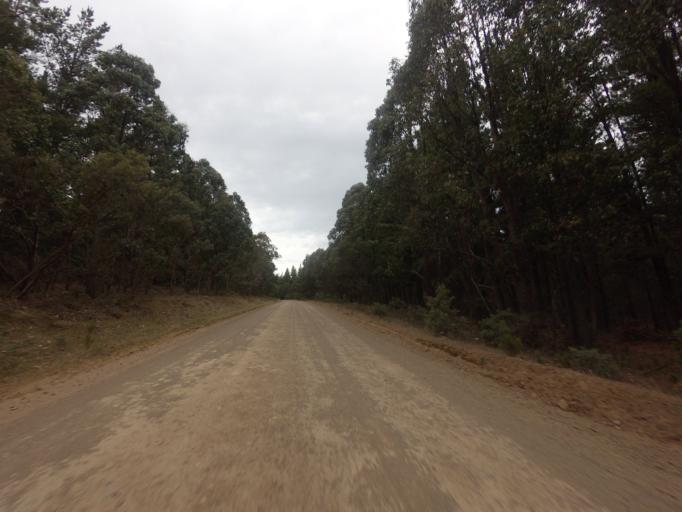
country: AU
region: Tasmania
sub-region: Derwent Valley
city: New Norfolk
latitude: -42.5704
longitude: 146.9876
